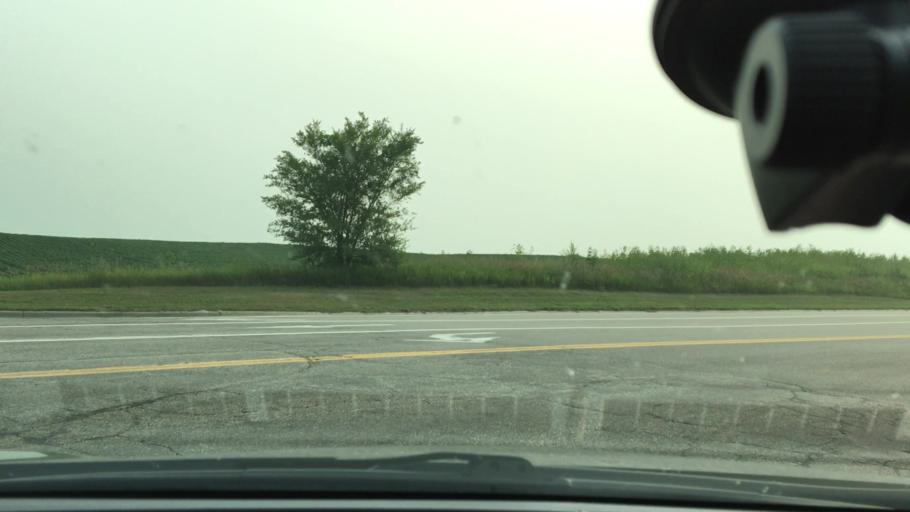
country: US
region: Minnesota
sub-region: Wright County
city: Otsego
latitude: 45.2525
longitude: -93.5914
